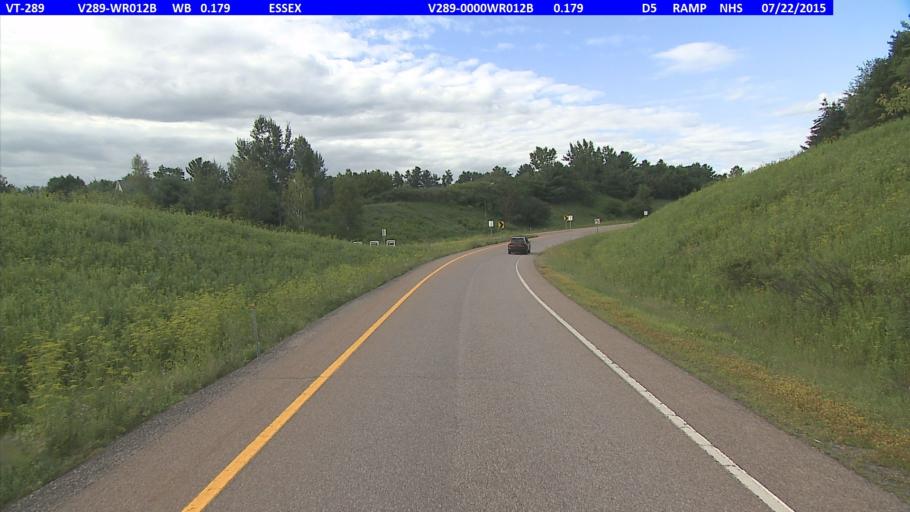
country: US
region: Vermont
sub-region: Chittenden County
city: Essex Junction
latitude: 44.4827
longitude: -73.0675
